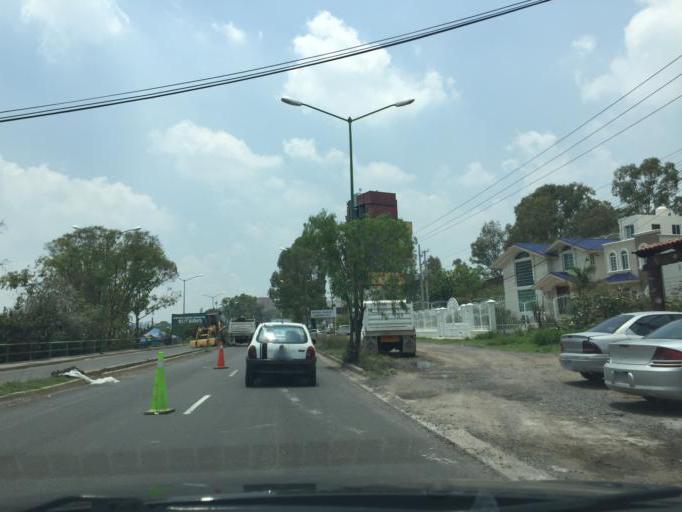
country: MX
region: Guanajuato
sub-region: Leon
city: La Ermita
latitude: 21.1647
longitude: -101.7272
